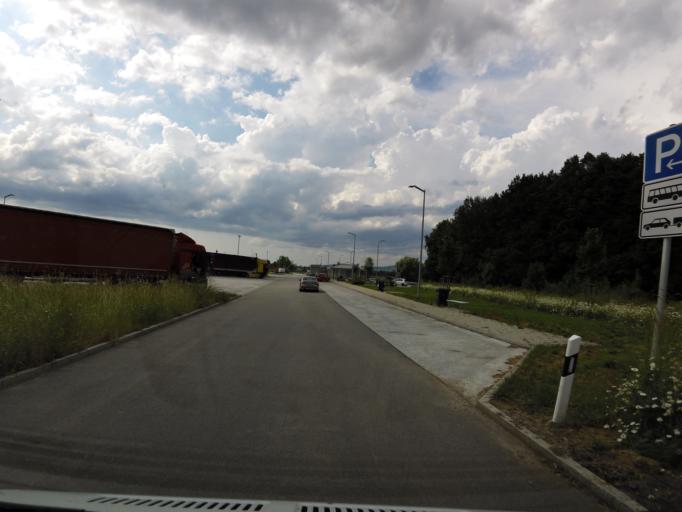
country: DE
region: Bavaria
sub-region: Lower Bavaria
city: Hengersberg
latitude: 48.7572
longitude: 13.0685
